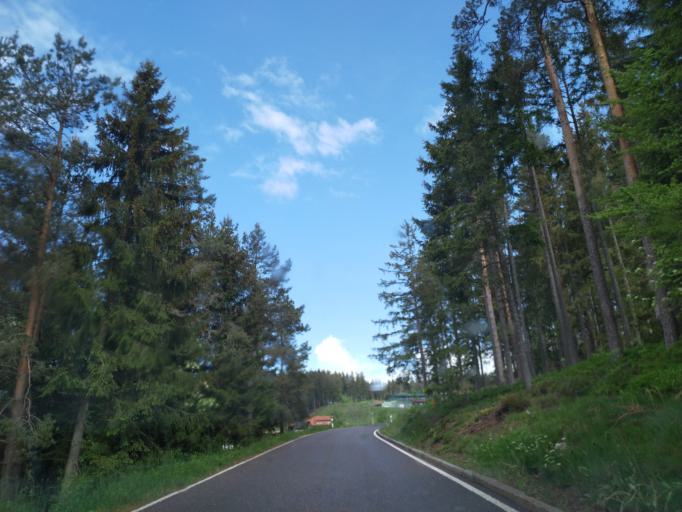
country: DE
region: Baden-Wuerttemberg
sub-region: Freiburg Region
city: Friedenweiler
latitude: 47.9353
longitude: 8.2519
